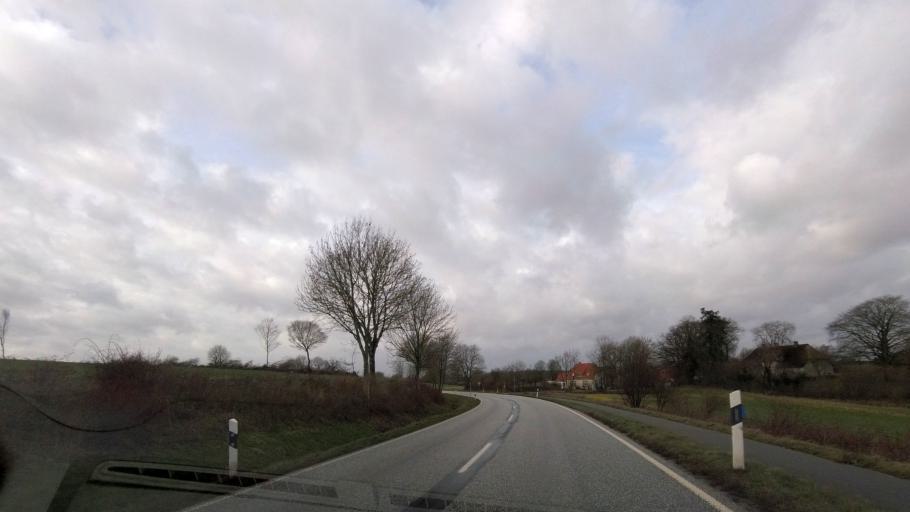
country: DE
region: Schleswig-Holstein
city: Rabenkirchen-Fauluck
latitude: 54.6453
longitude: 9.8523
